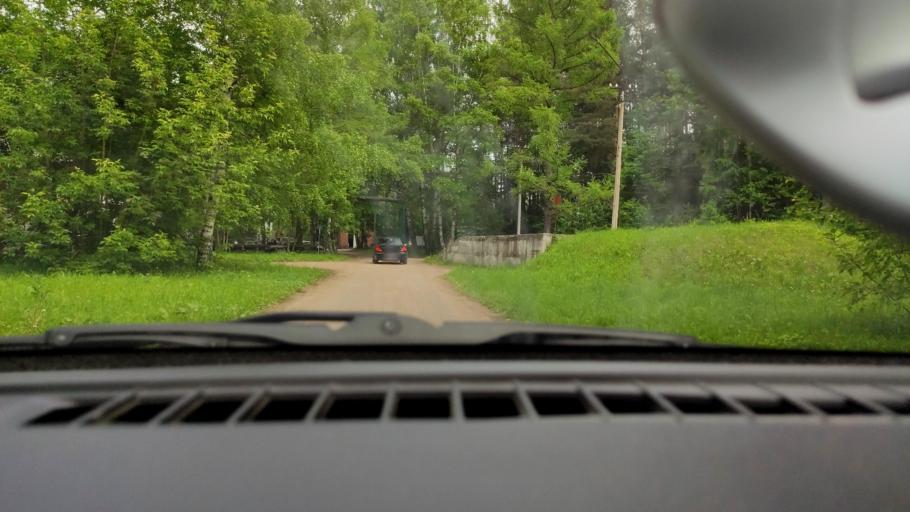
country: RU
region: Perm
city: Kondratovo
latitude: 57.9763
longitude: 56.1473
